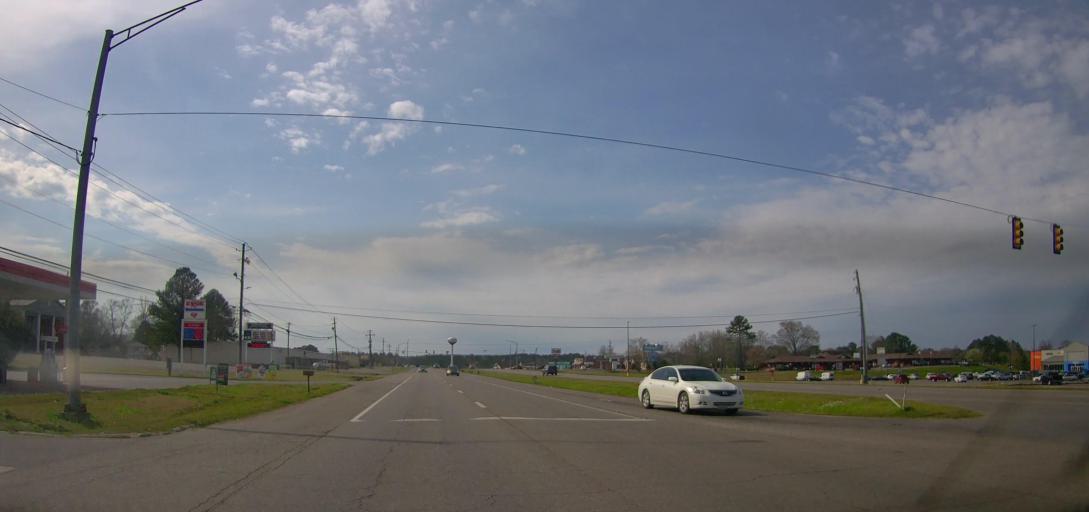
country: US
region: Alabama
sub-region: Walker County
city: Sumiton
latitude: 33.7430
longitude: -87.0424
